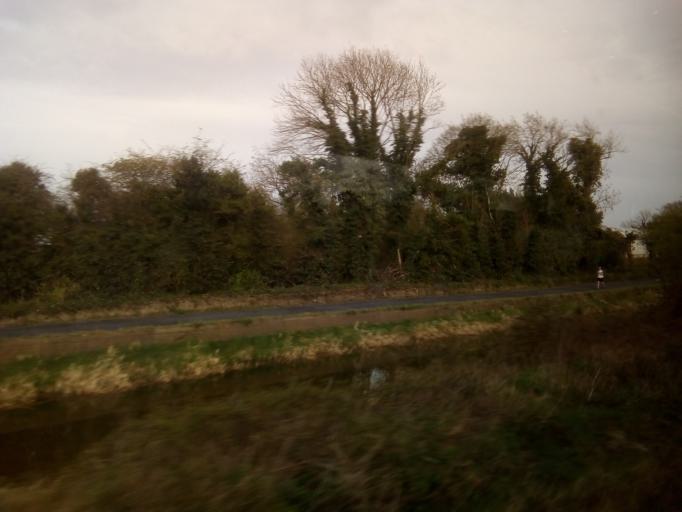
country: IE
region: Leinster
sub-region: Kildare
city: Kilcock
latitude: 53.3881
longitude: -6.6402
